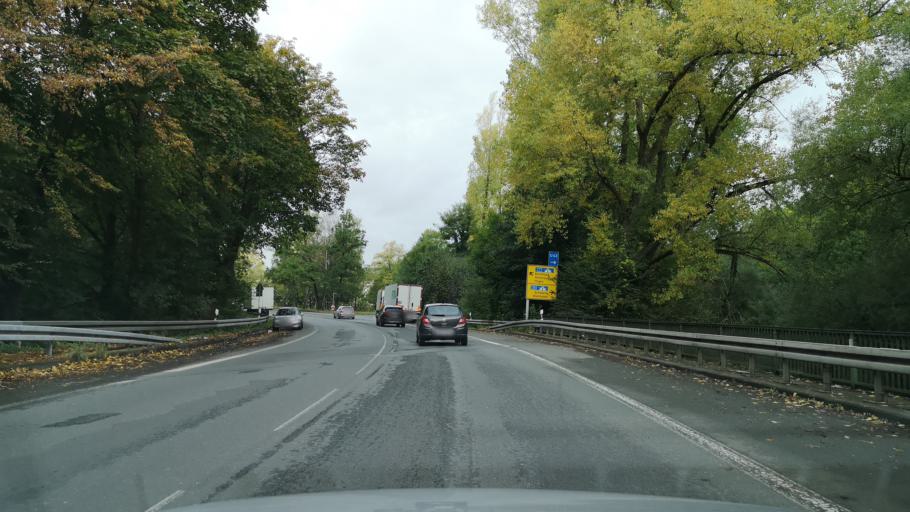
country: DE
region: North Rhine-Westphalia
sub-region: Regierungsbezirk Arnsberg
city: Hagen
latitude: 51.4040
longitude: 7.4983
